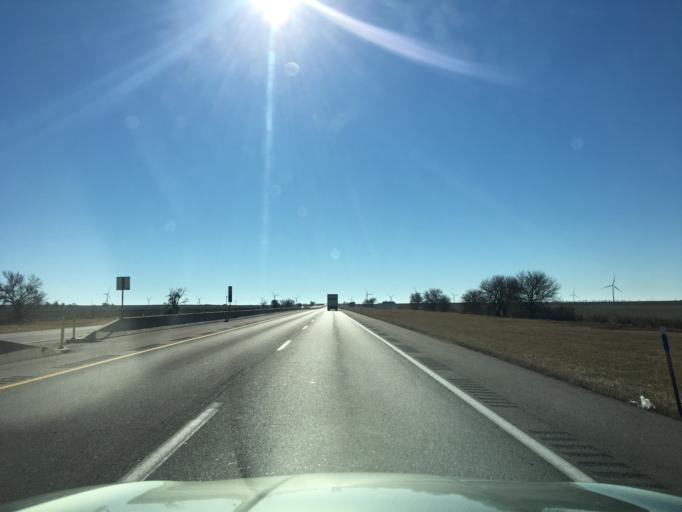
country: US
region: Kansas
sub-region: Sumner County
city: Wellington
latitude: 37.1789
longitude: -97.3396
